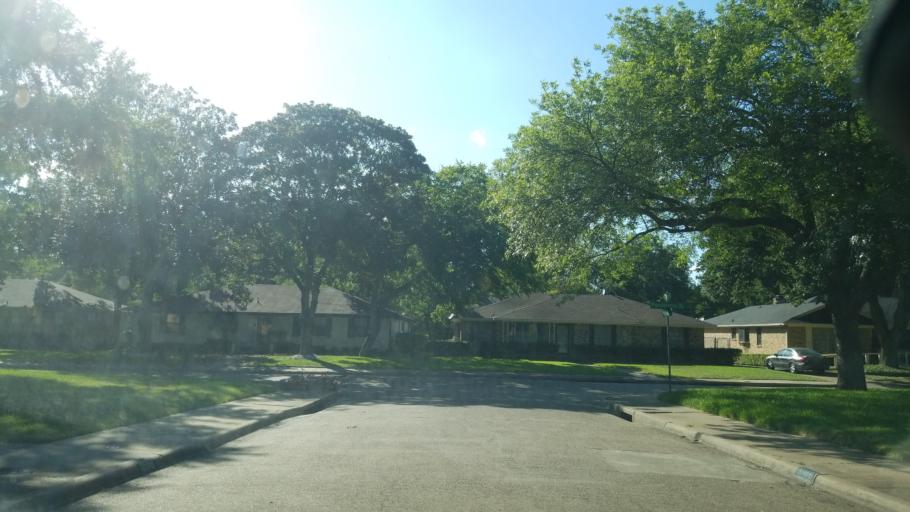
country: US
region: Texas
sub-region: Dallas County
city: Highland Park
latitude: 32.7876
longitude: -96.7047
